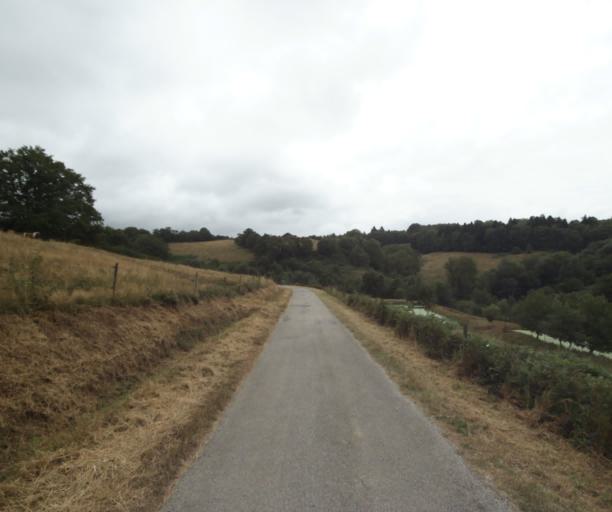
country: FR
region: Midi-Pyrenees
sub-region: Departement du Tarn
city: Soreze
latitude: 43.4127
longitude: 2.0840
